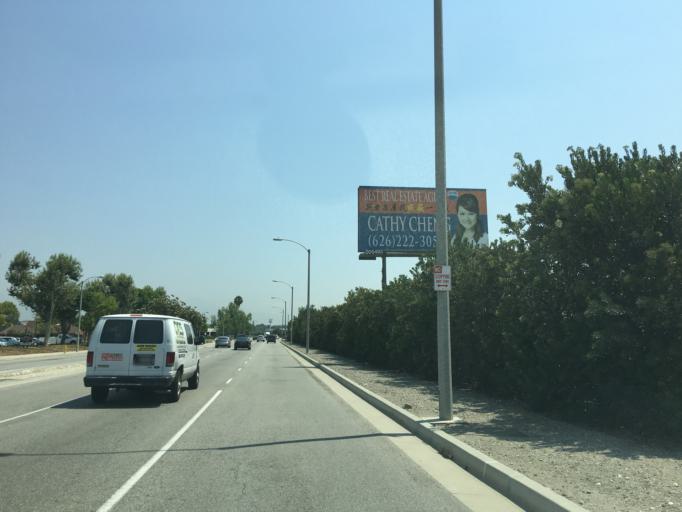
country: US
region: California
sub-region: Los Angeles County
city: Walnut
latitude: 34.0108
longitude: -117.8570
